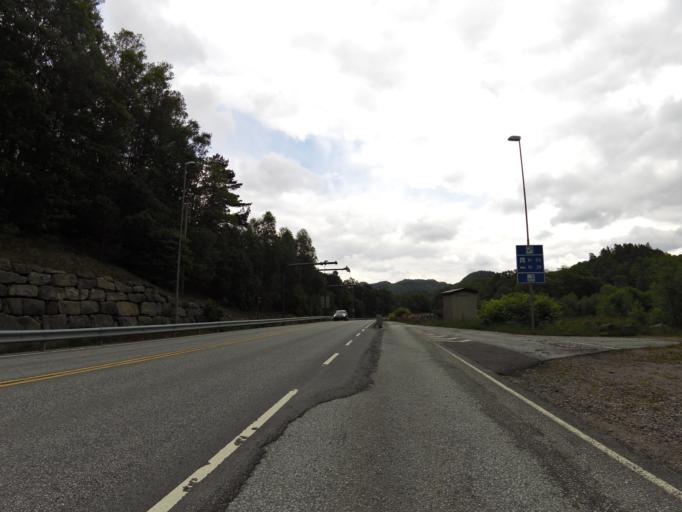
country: NO
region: Vest-Agder
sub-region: Lyngdal
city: Lyngdal
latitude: 58.1124
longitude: 6.9406
